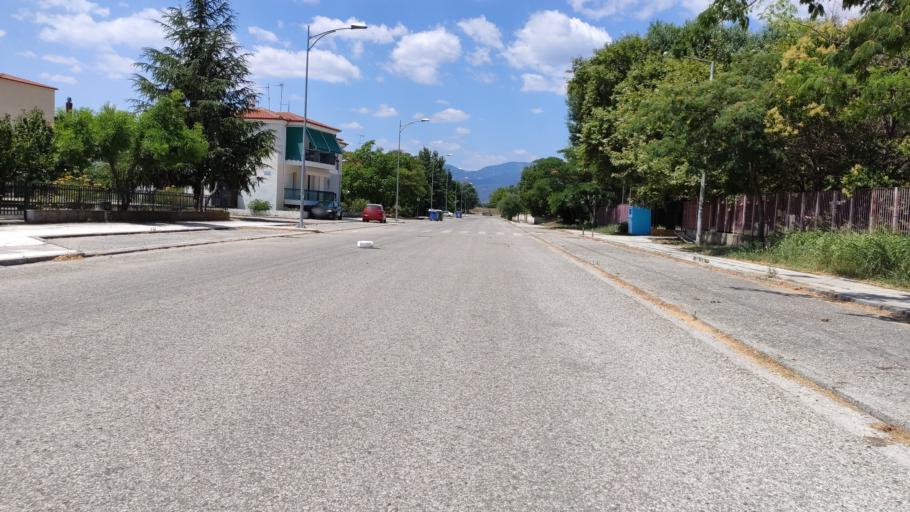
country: GR
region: East Macedonia and Thrace
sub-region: Nomos Rodopis
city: Komotini
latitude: 41.1263
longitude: 25.3970
